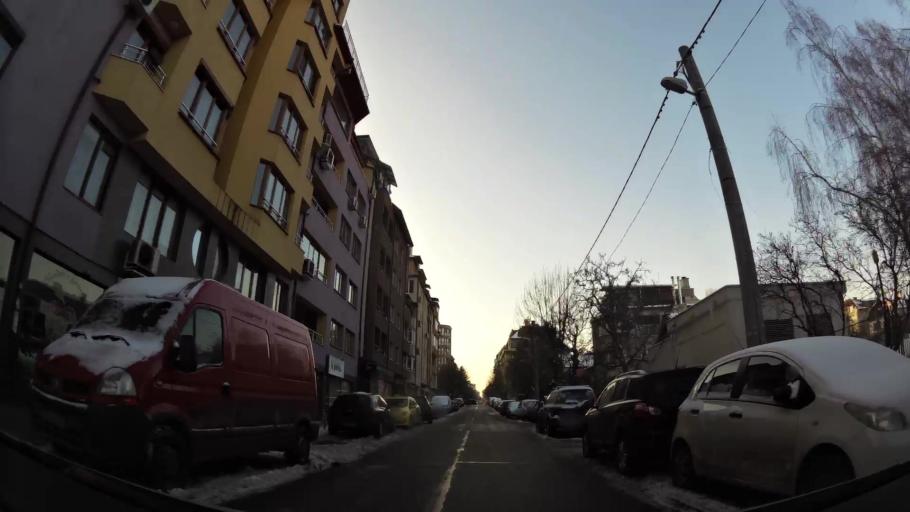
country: BG
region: Sofia-Capital
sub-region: Stolichna Obshtina
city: Sofia
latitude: 42.6892
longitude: 23.3621
